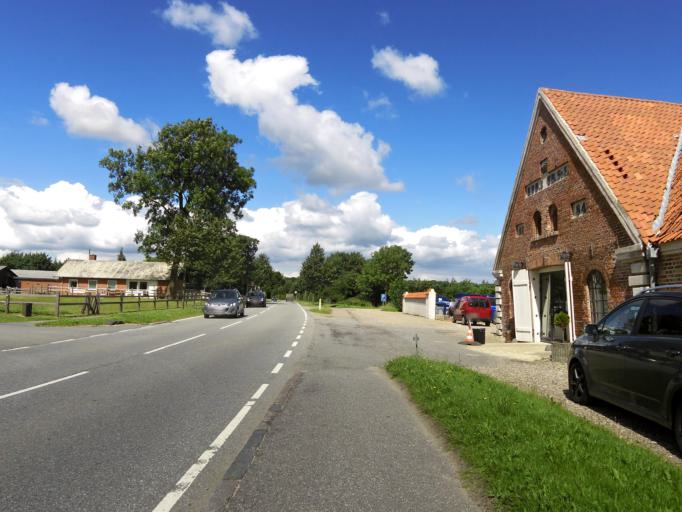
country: DK
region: South Denmark
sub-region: Haderslev Kommune
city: Gram
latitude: 55.2969
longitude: 9.0590
